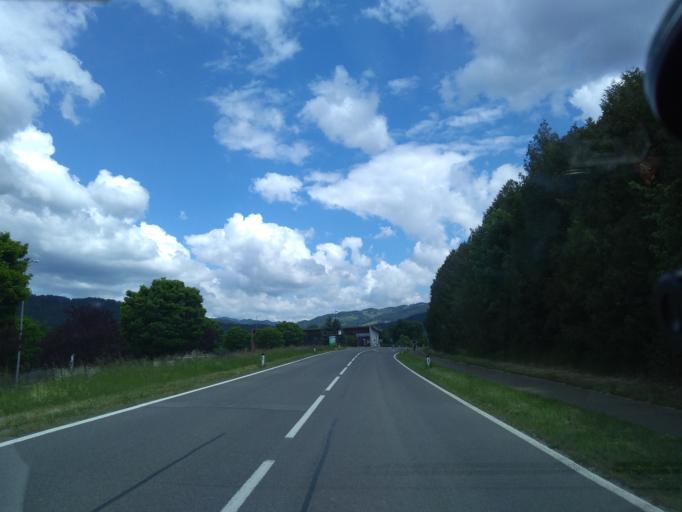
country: AT
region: Styria
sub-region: Politischer Bezirk Graz-Umgebung
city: Frohnleiten
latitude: 47.2569
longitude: 15.3208
